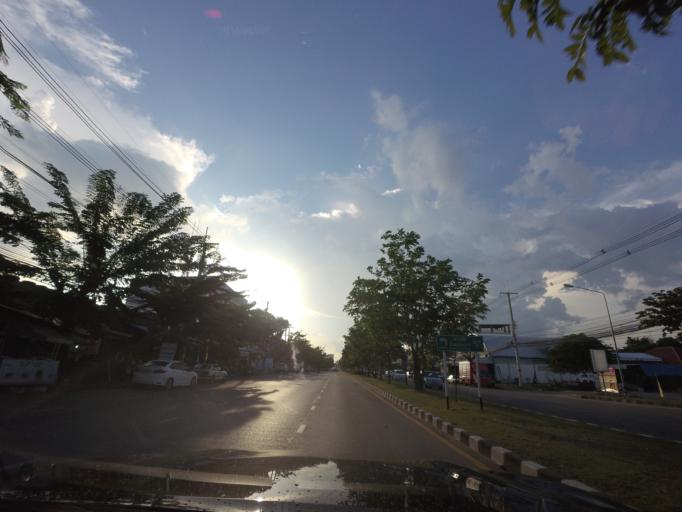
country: TH
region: Khon Kaen
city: Khon Kaen
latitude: 16.4281
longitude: 102.8593
